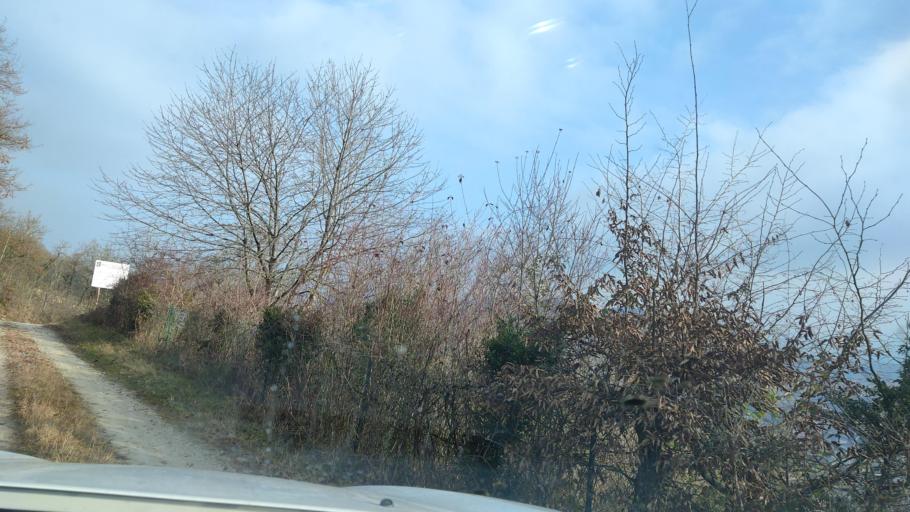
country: FR
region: Rhone-Alpes
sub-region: Departement de la Savoie
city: Gresy-sur-Aix
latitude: 45.7205
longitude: 5.9122
